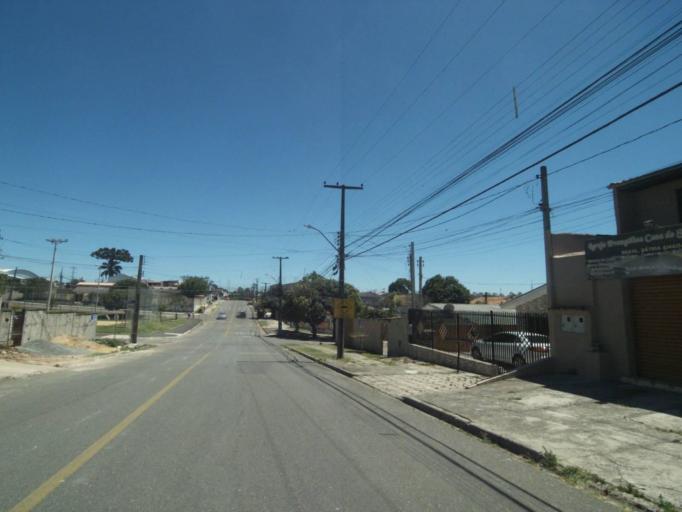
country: BR
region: Parana
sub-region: Curitiba
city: Curitiba
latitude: -25.4759
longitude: -49.3490
